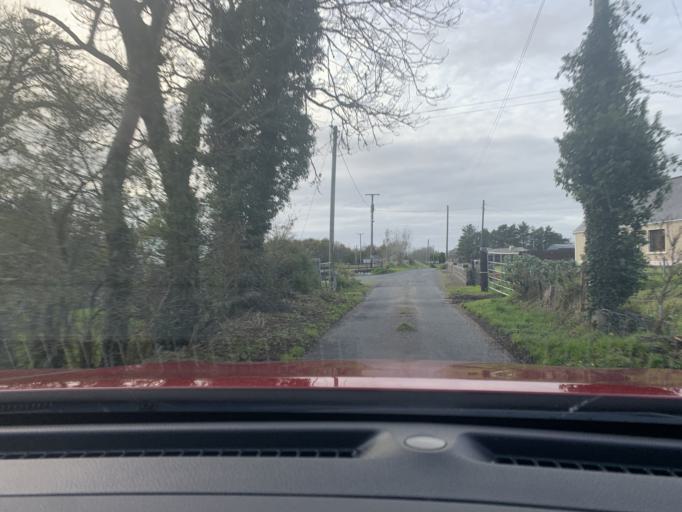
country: IE
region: Connaught
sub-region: Roscommon
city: Ballaghaderreen
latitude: 53.9697
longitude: -8.6191
